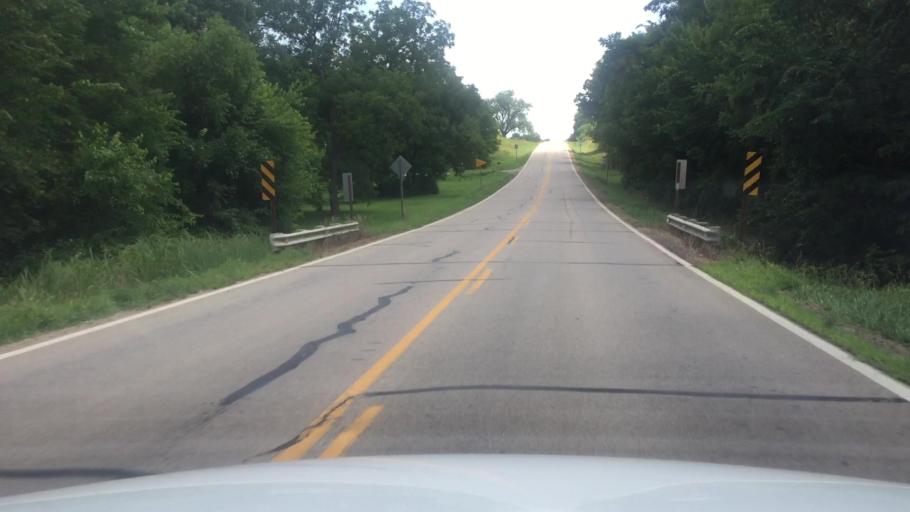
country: US
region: Kansas
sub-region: Brown County
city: Horton
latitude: 39.6674
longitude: -95.6362
